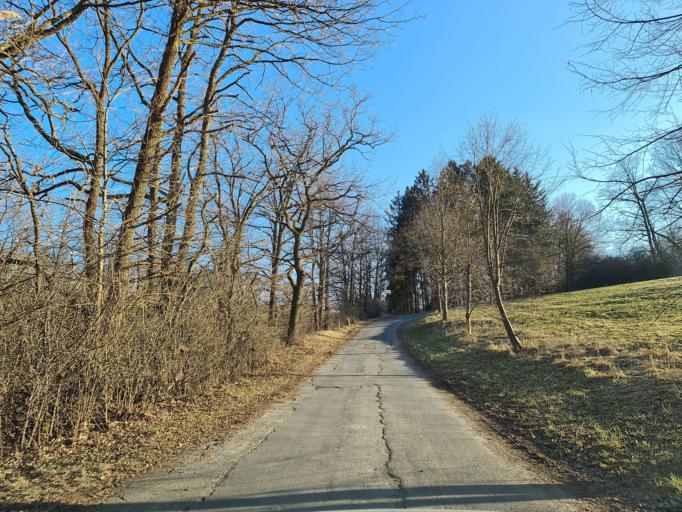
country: DE
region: Saxony
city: Pohl
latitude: 50.5361
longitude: 12.1722
